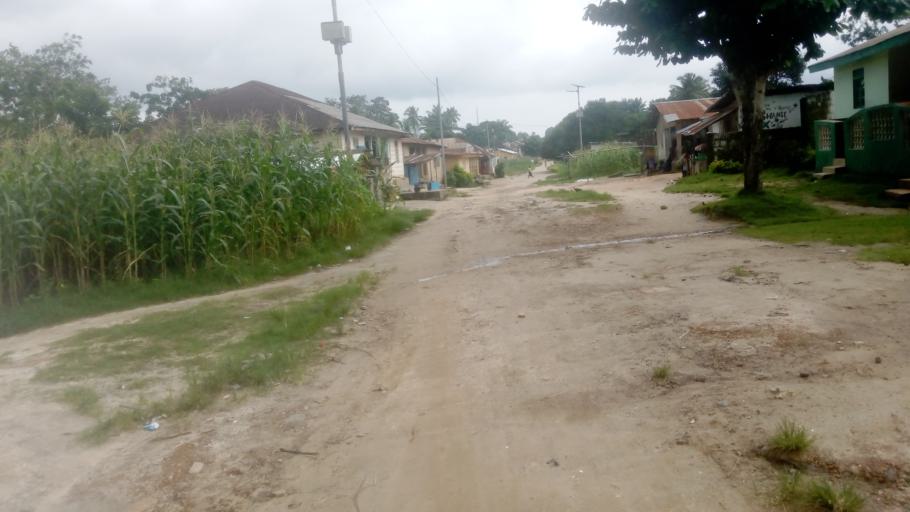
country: SL
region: Northern Province
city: Lunsar
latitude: 8.6811
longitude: -12.5388
